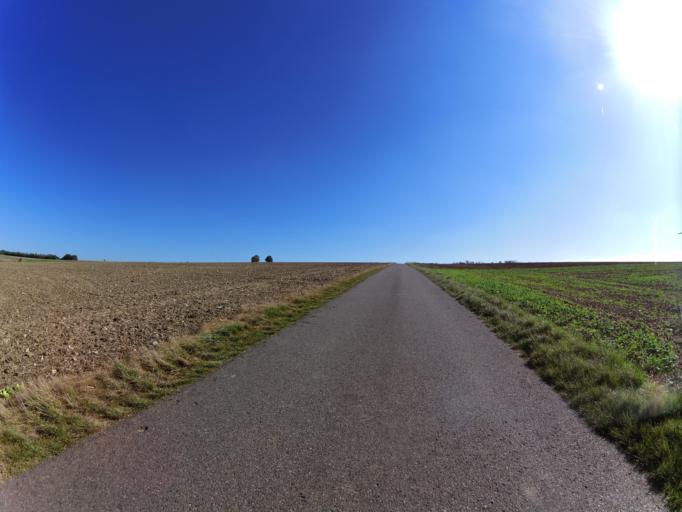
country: DE
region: Bavaria
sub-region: Regierungsbezirk Unterfranken
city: Waldbrunn
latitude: 49.7164
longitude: 9.7767
